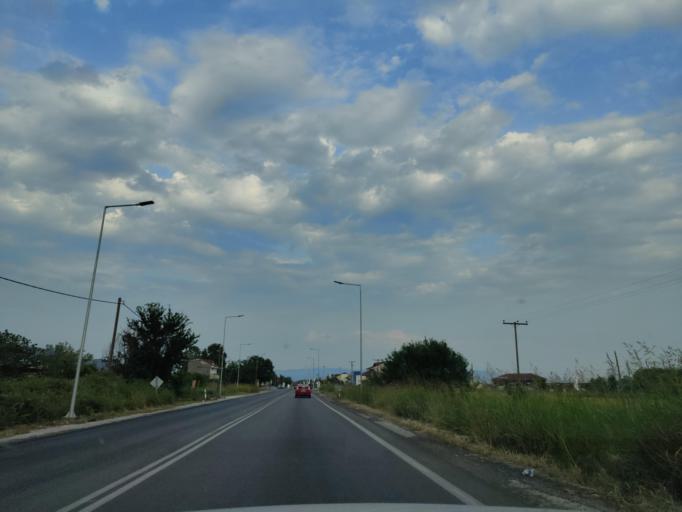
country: GR
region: East Macedonia and Thrace
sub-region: Nomos Dramas
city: Xiropotamos
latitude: 41.1575
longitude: 24.1002
